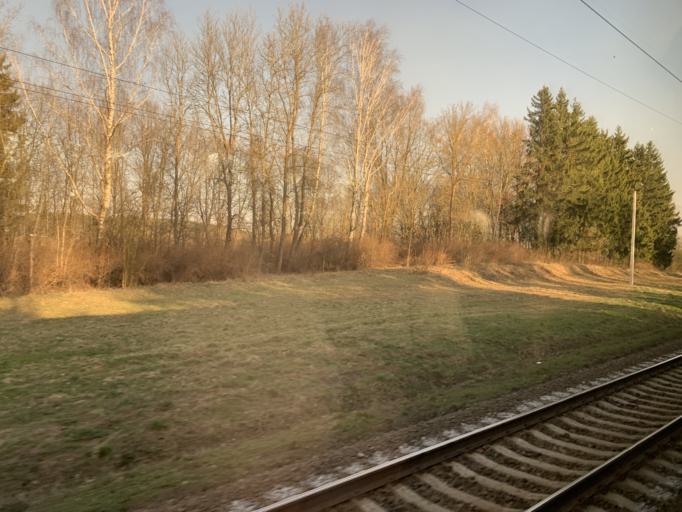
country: BY
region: Minsk
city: Zaslawye
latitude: 53.9982
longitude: 27.2831
